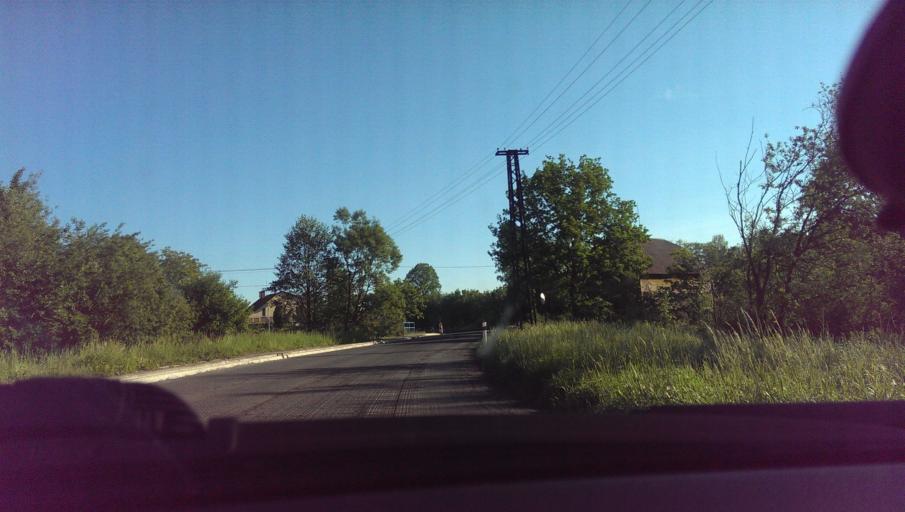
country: CZ
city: Frydlant nad Ostravici
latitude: 49.5757
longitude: 18.3587
